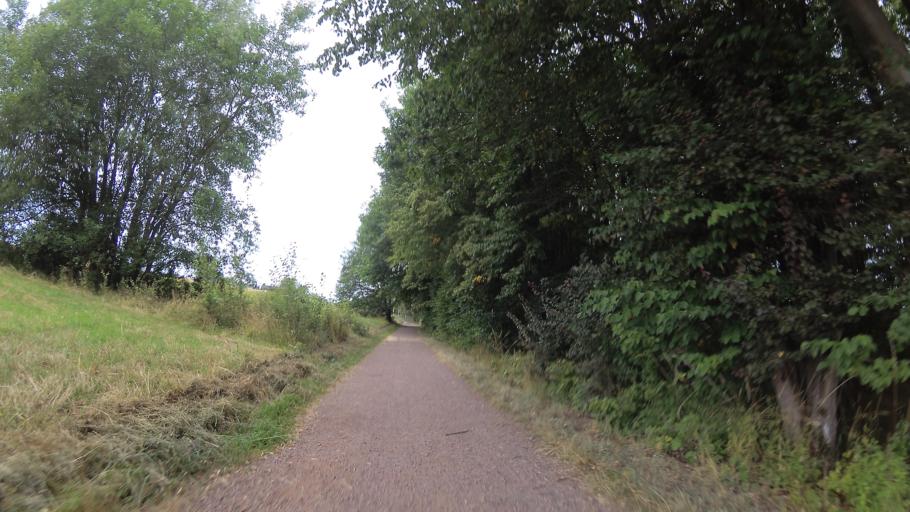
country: DE
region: Saarland
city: Schwalbach
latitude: 49.3103
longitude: 6.8120
